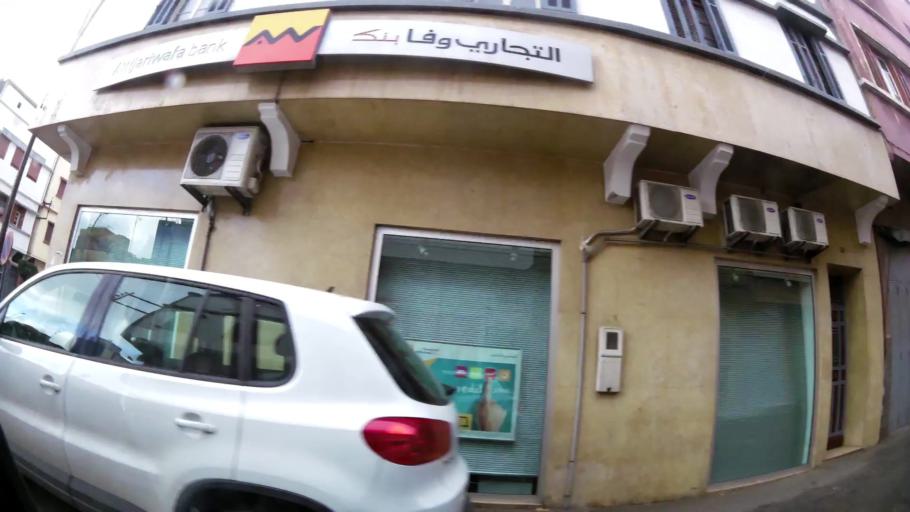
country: MA
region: Grand Casablanca
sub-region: Casablanca
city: Casablanca
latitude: 33.5498
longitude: -7.5794
